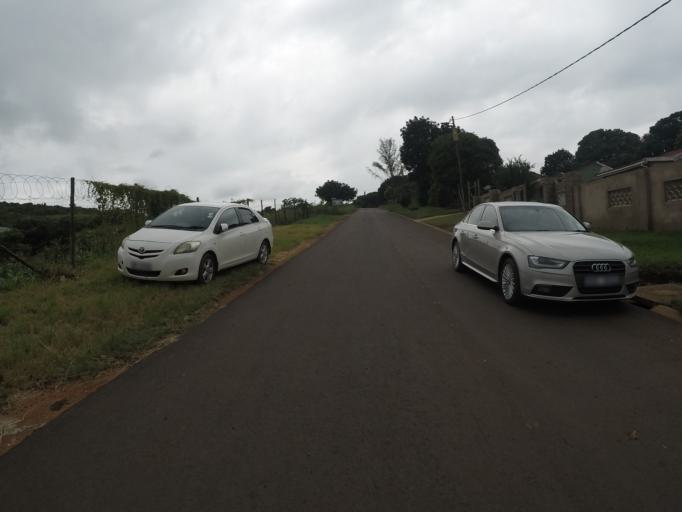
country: ZA
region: KwaZulu-Natal
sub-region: uThungulu District Municipality
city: Empangeni
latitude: -28.7727
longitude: 31.8605
